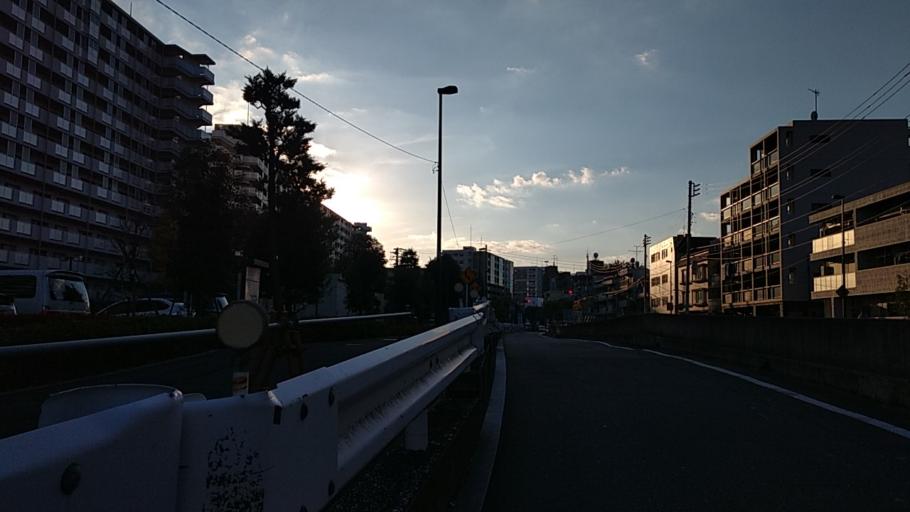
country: JP
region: Tokyo
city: Tokyo
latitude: 35.7095
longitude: 139.7012
